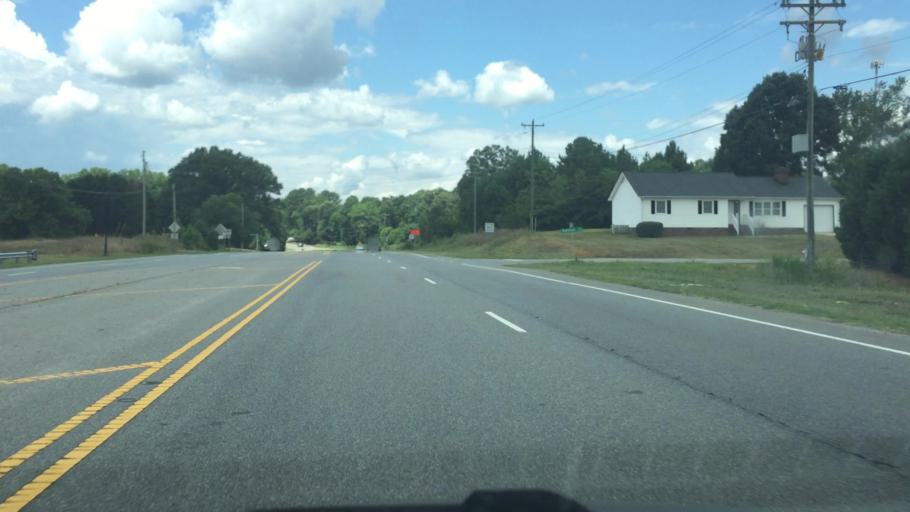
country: US
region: North Carolina
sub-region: Rowan County
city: Enochville
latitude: 35.4902
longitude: -80.6723
